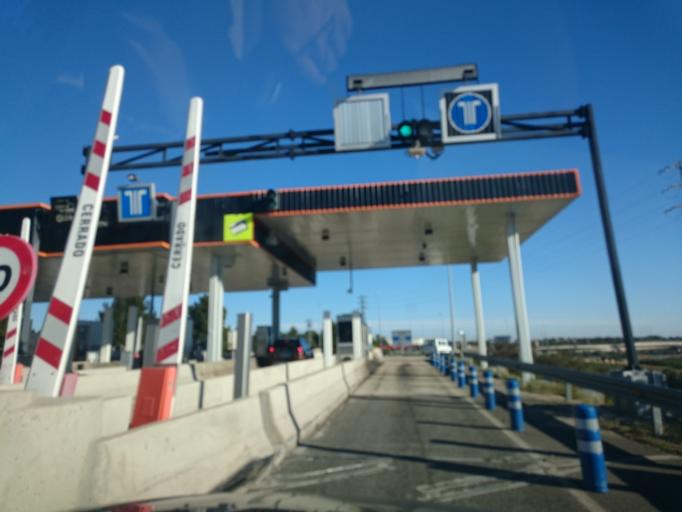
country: ES
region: Catalonia
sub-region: Provincia de Tarragona
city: Colldejou
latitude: 41.0035
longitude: 0.9125
